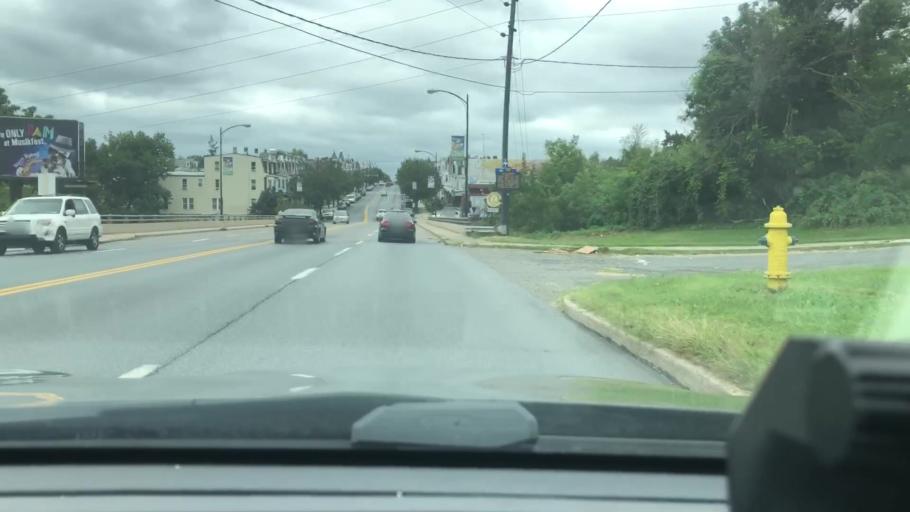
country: US
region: Pennsylvania
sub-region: Lehigh County
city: Allentown
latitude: 40.6175
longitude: -75.4790
